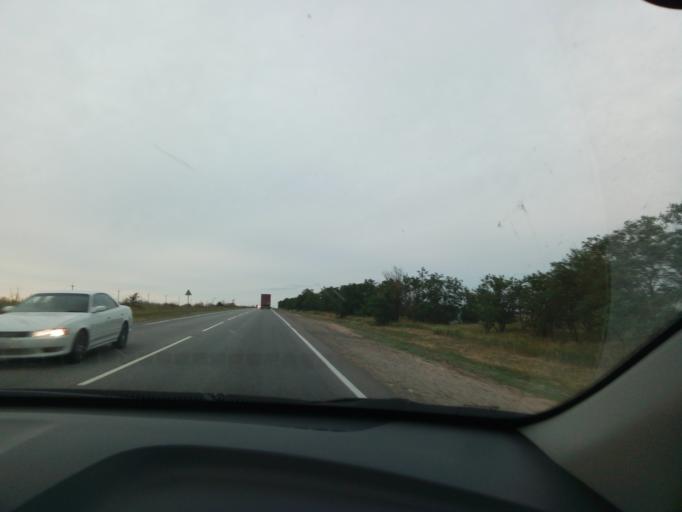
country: RU
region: Volgograd
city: Dubovka
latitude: 49.1413
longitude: 44.8278
